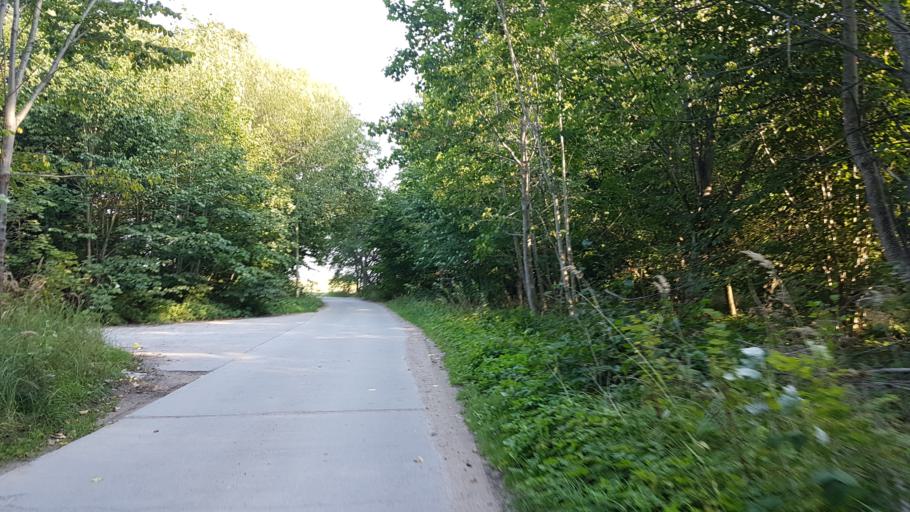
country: DE
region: Mecklenburg-Vorpommern
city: Sagard
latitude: 54.5022
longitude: 13.5337
